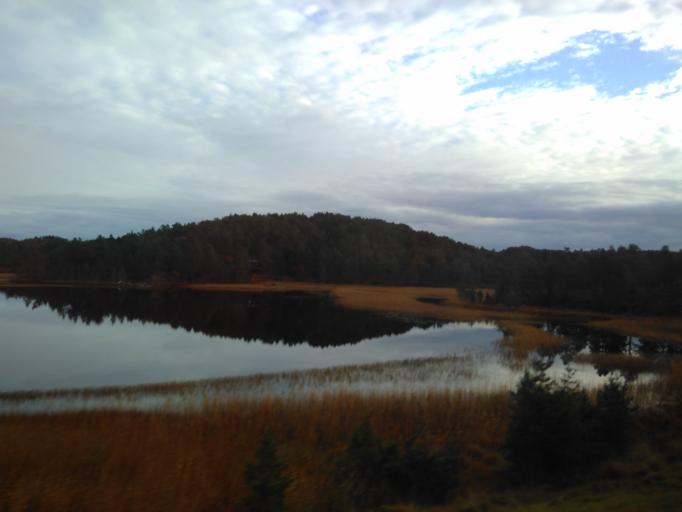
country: NO
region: Sor-Trondelag
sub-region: Hitra
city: Fillan
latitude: 63.5612
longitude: 9.0469
